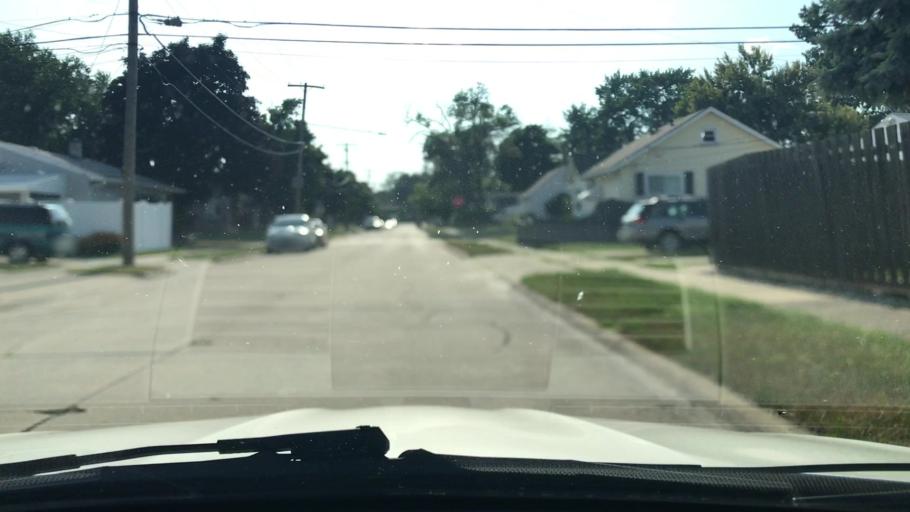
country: US
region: Michigan
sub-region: Oakland County
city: Clawson
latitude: 42.5346
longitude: -83.1564
